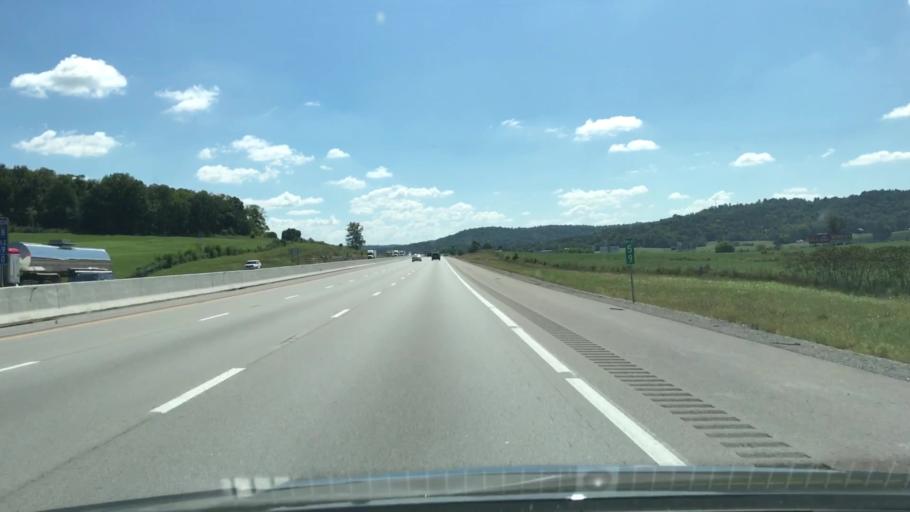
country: US
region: Kentucky
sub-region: Hart County
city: Horse Cave
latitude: 37.2225
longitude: -85.9358
